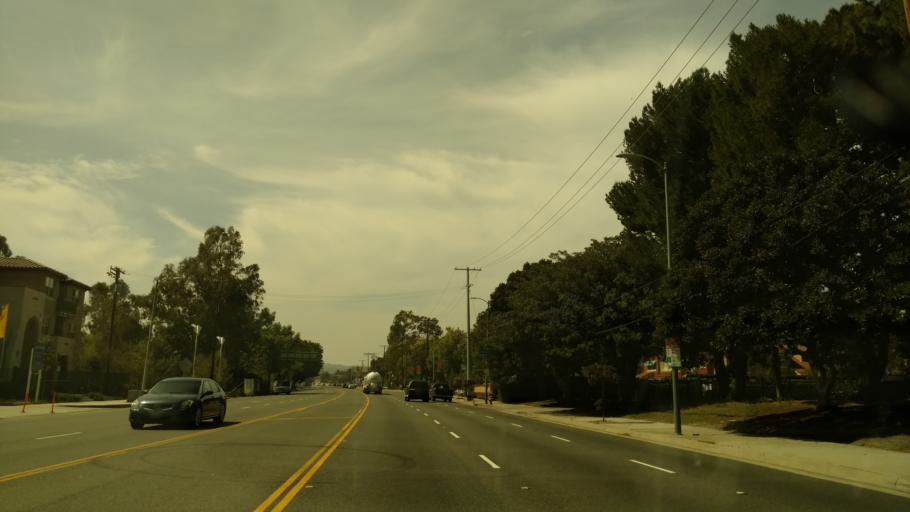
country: US
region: California
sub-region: Los Angeles County
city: Lomita
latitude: 33.7909
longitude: -118.2850
